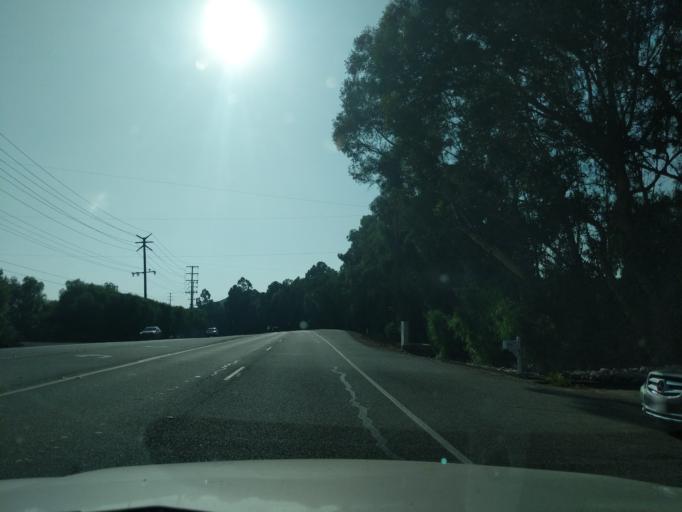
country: US
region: California
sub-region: Ventura County
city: Moorpark
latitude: 34.2687
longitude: -118.8458
